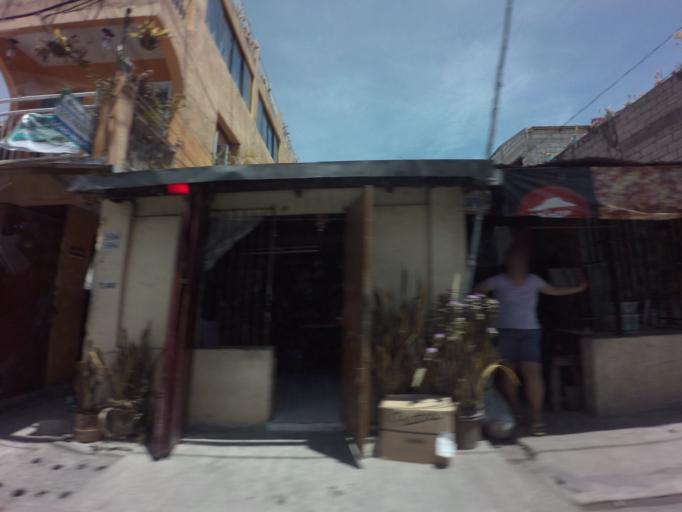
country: PH
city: Sambayanihan People's Village
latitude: 14.4584
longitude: 121.0535
